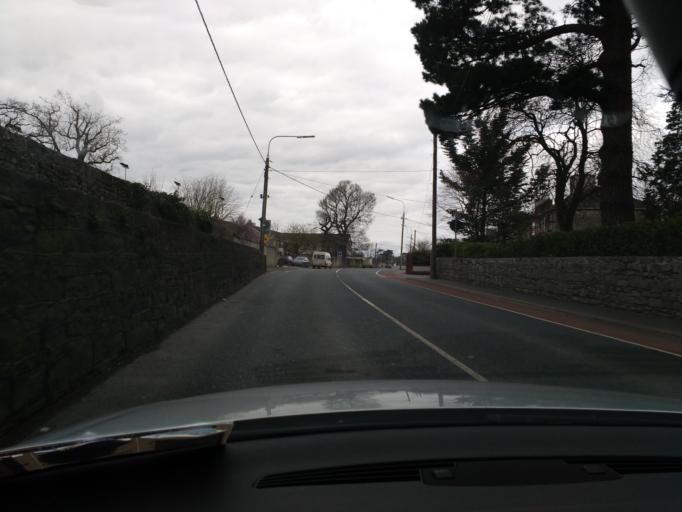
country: IE
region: Leinster
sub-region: Kilkenny
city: Kilkenny
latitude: 52.6596
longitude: -7.2588
